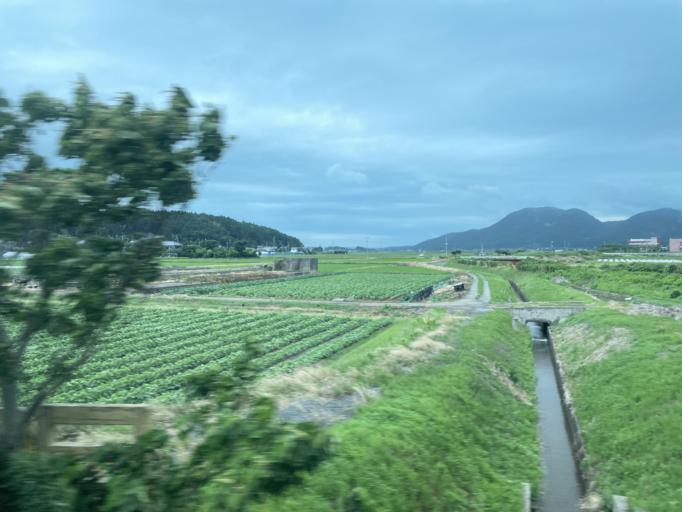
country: JP
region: Niigata
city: Yoshida-kasugacho
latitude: 37.6985
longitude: 138.8427
